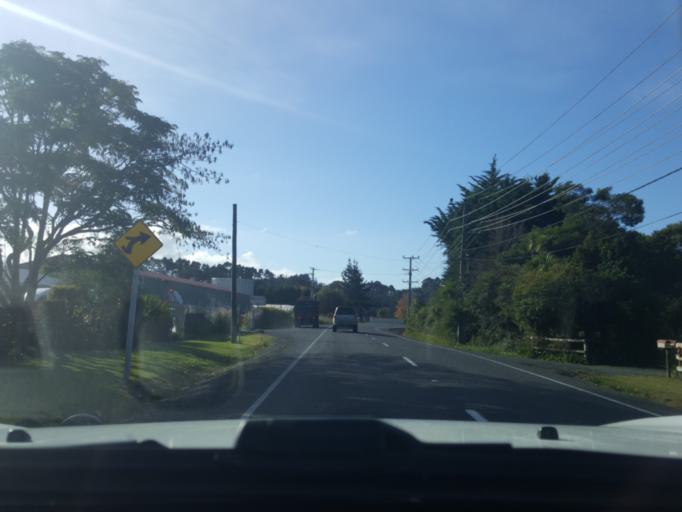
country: NZ
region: Auckland
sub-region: Auckland
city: Muriwai Beach
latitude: -36.7642
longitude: 174.5768
